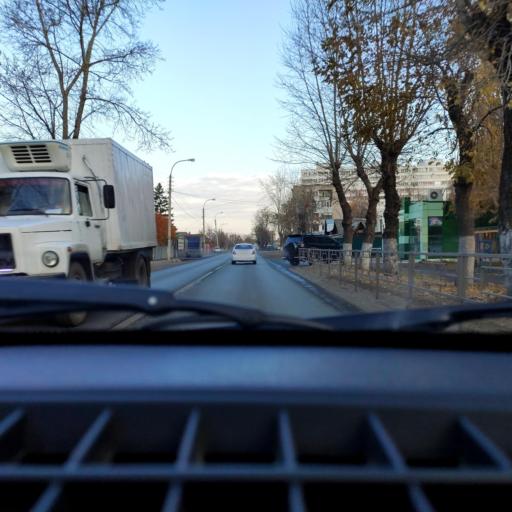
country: RU
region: Bashkortostan
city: Avdon
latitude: 54.6990
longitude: 55.8240
